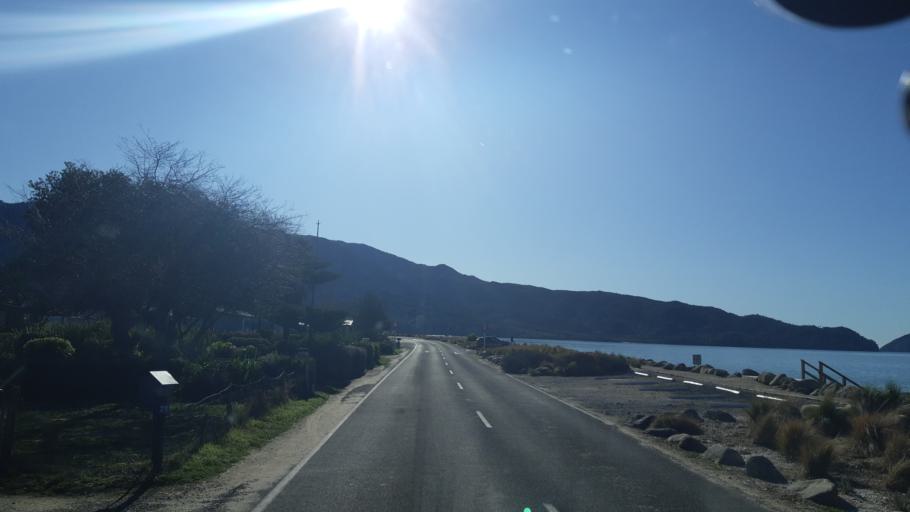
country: NZ
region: Tasman
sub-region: Tasman District
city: Motueka
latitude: -41.0067
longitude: 173.0093
